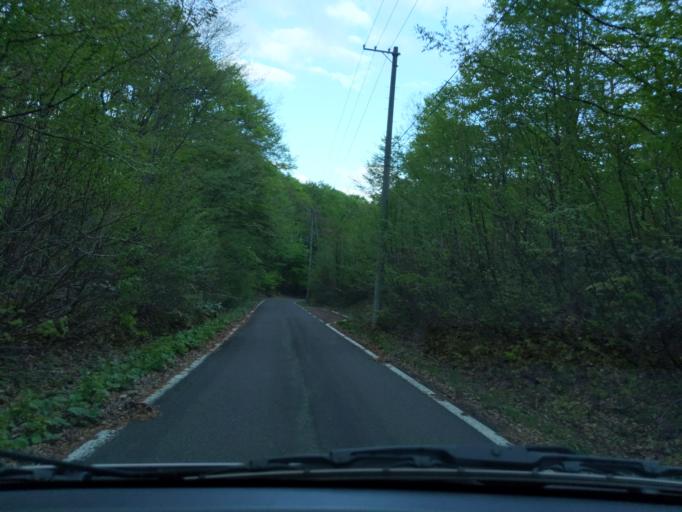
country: JP
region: Iwate
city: Ichinoseki
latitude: 38.9040
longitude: 140.8375
